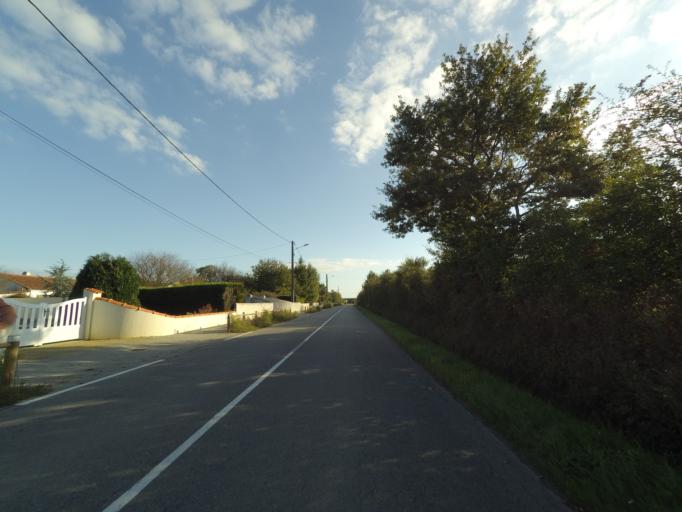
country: FR
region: Pays de la Loire
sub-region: Departement de la Loire-Atlantique
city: Chemere
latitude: 47.1302
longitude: -1.9106
